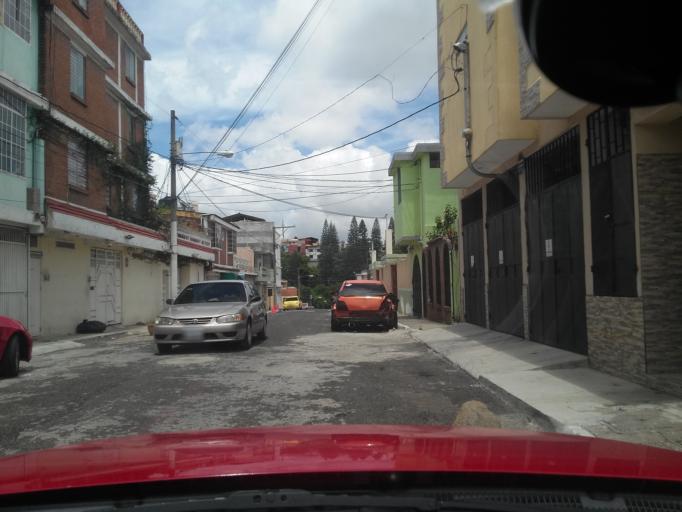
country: GT
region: Guatemala
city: Mixco
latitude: 14.6465
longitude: -90.5665
